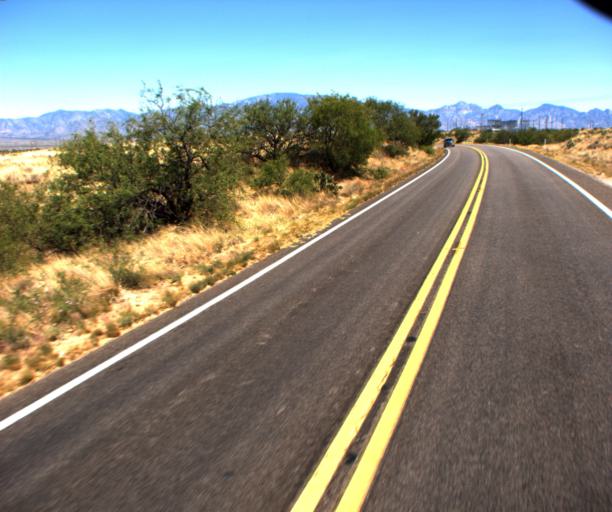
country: US
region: Arizona
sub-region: Pima County
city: Catalina
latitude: 32.6070
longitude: -110.9860
